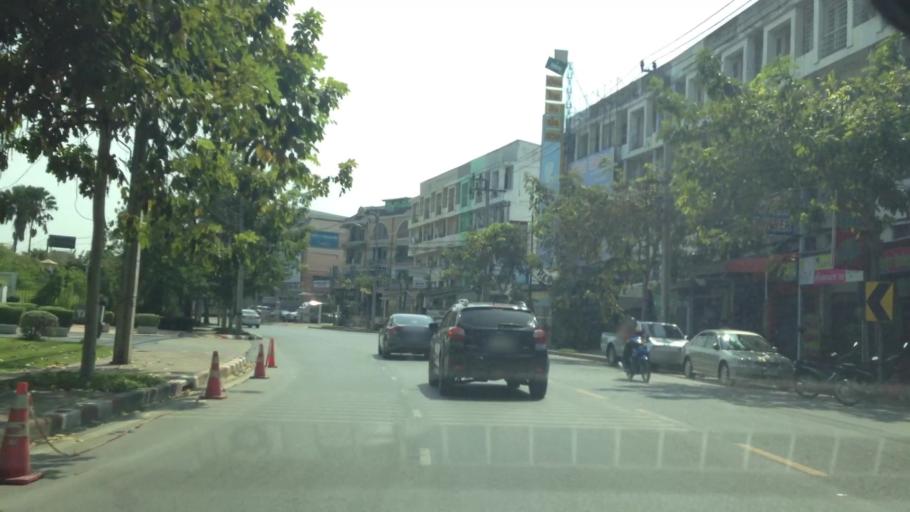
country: TH
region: Bangkok
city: Bang Khen
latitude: 13.8948
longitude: 100.6383
